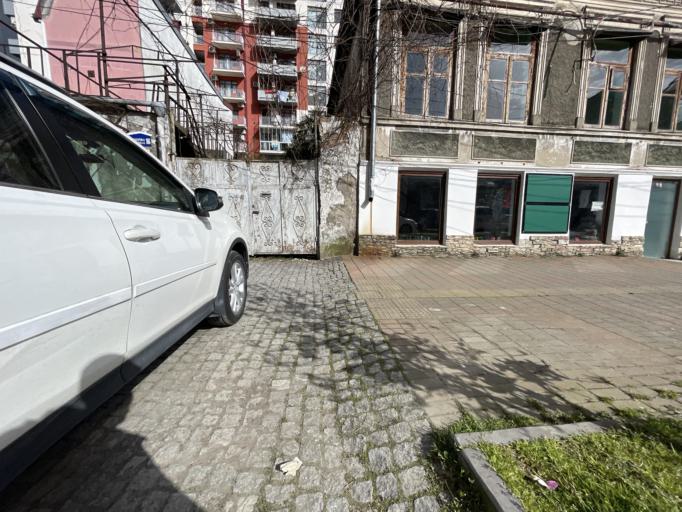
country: GE
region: Ajaria
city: Batumi
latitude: 41.6449
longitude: 41.6303
